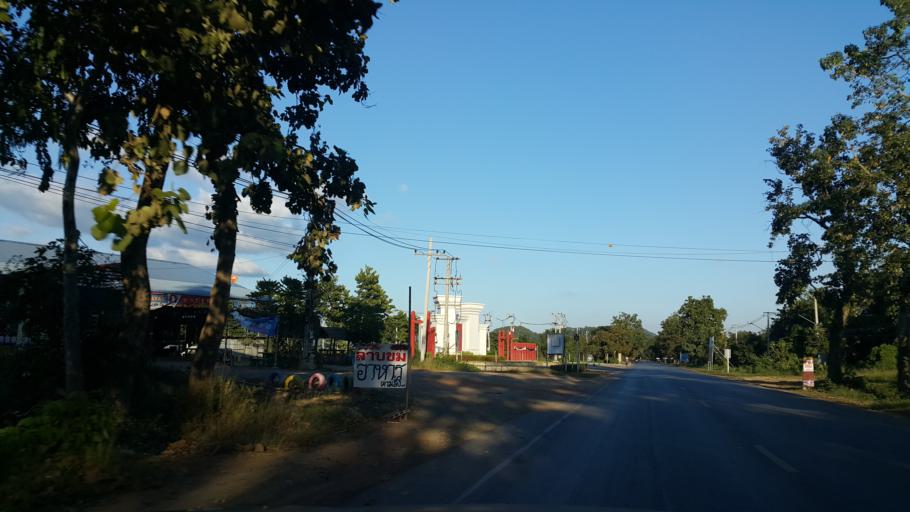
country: TH
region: Sukhothai
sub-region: Amphoe Si Satchanalai
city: Si Satchanalai
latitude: 17.5514
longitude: 99.8659
